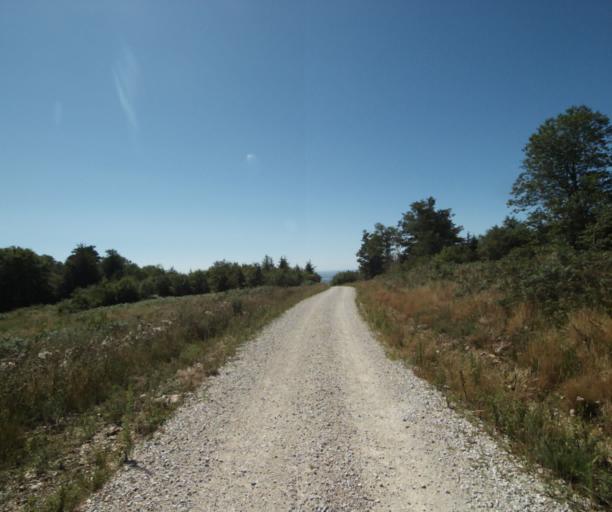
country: FR
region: Midi-Pyrenees
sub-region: Departement du Tarn
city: Soreze
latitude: 43.4395
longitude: 2.1108
